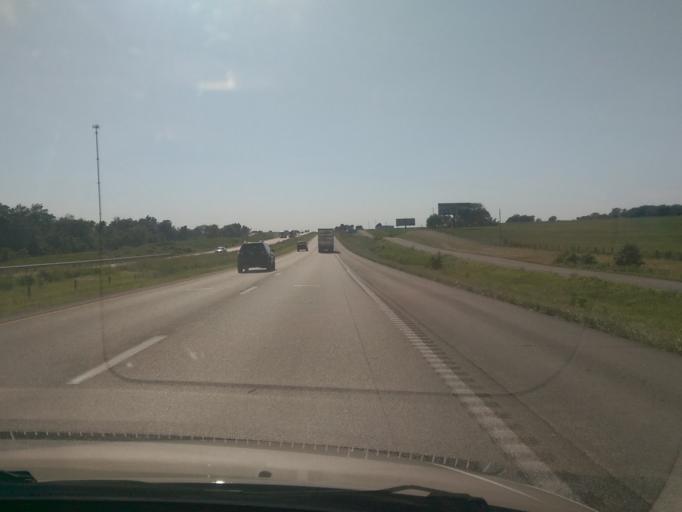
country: US
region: Missouri
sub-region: Saline County
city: Sweet Springs
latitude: 38.9764
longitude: -93.3964
